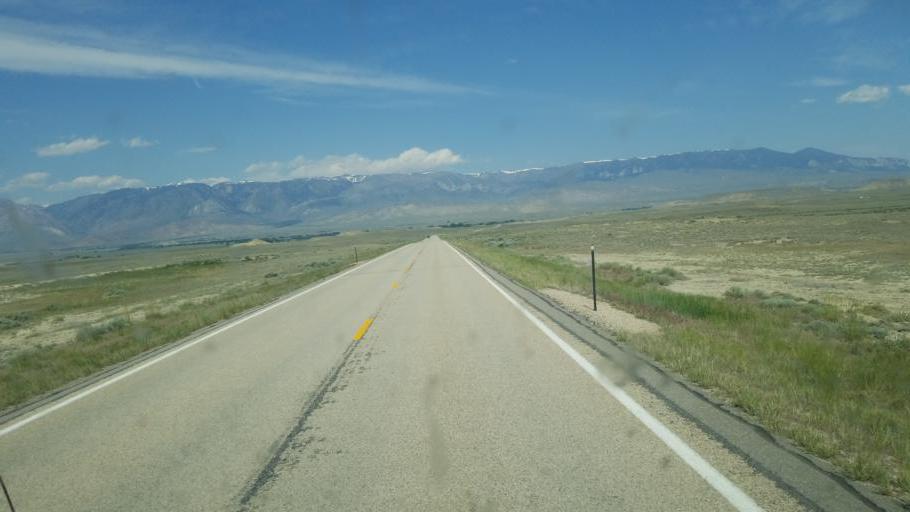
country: US
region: Montana
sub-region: Carbon County
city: Red Lodge
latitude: 44.8877
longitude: -109.0747
